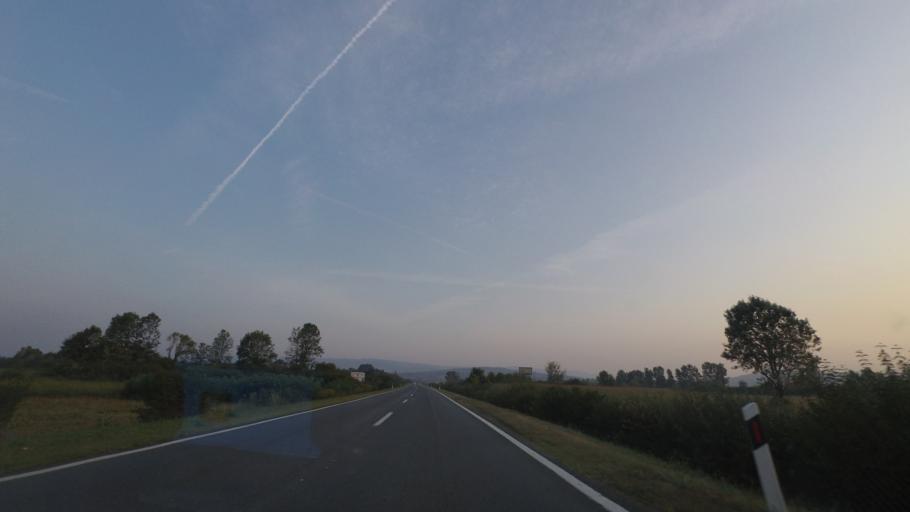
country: HR
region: Brodsko-Posavska
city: Nova Gradiska
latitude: 45.2377
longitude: 17.4106
